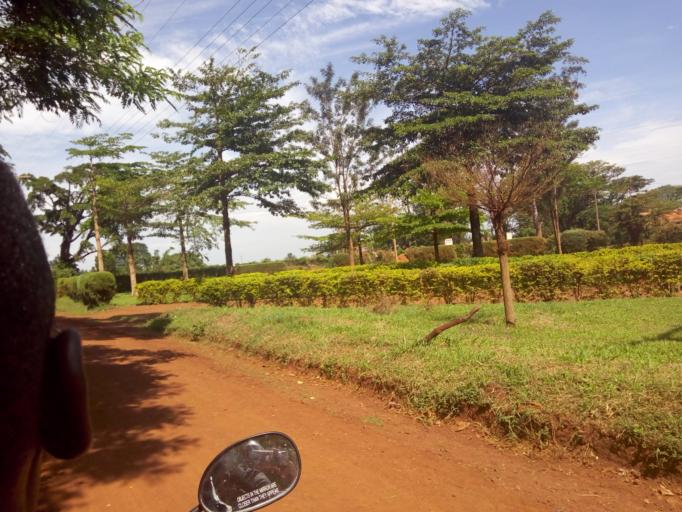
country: UG
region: Western Region
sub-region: Masindi District
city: Masindi
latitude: 1.6936
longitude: 31.7190
